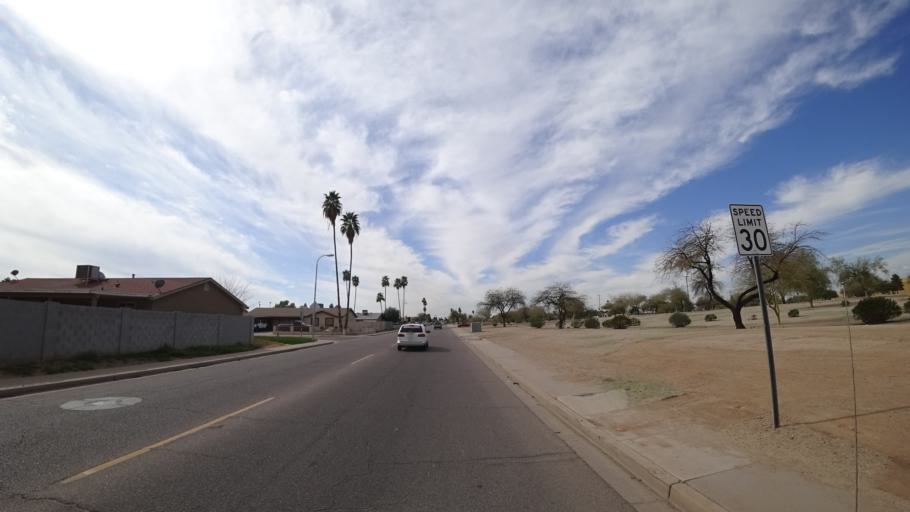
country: US
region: Arizona
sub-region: Maricopa County
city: Tolleson
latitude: 33.4732
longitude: -112.1997
